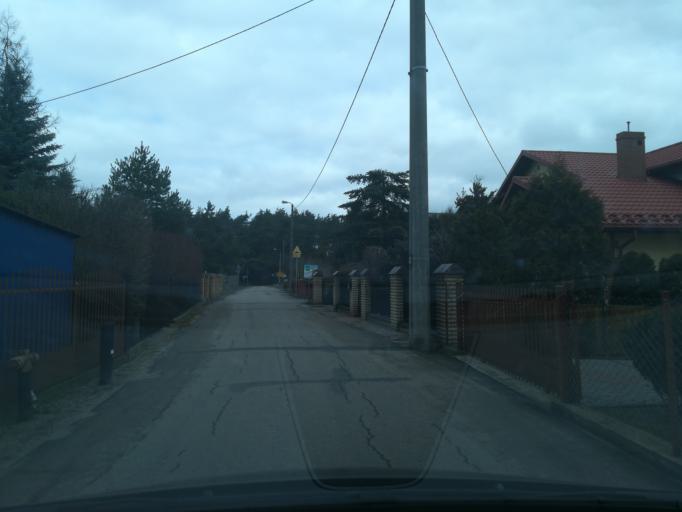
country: PL
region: Kujawsko-Pomorskie
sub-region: Powiat aleksandrowski
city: Ciechocinek
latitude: 52.8738
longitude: 18.7563
